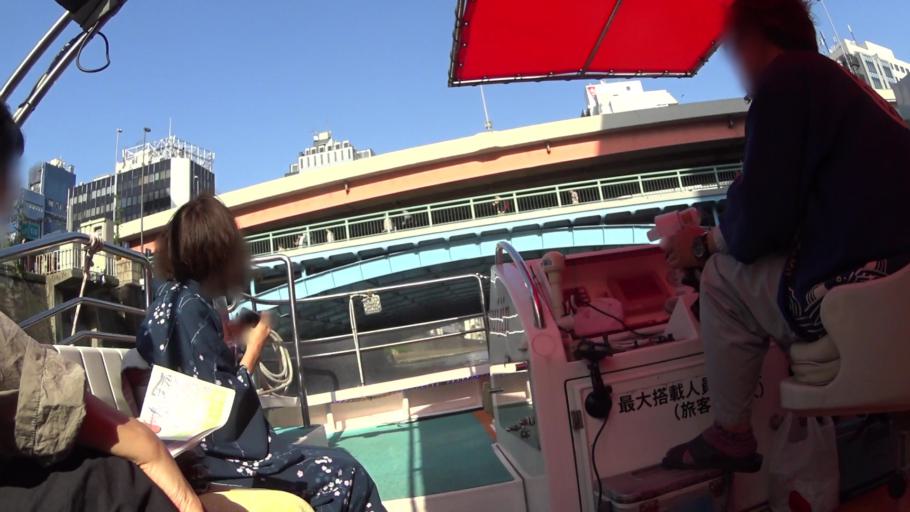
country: JP
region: Tokyo
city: Tokyo
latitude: 35.6734
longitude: 139.7864
